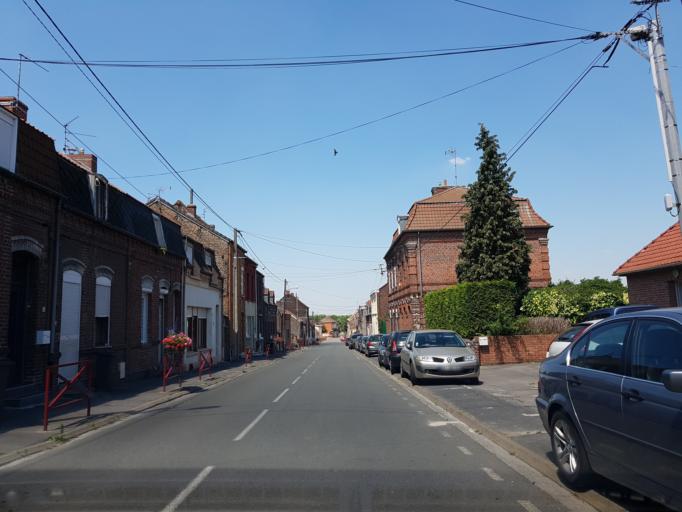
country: FR
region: Nord-Pas-de-Calais
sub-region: Departement du Nord
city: Neuville-sur-Escaut
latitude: 50.2986
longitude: 3.3559
